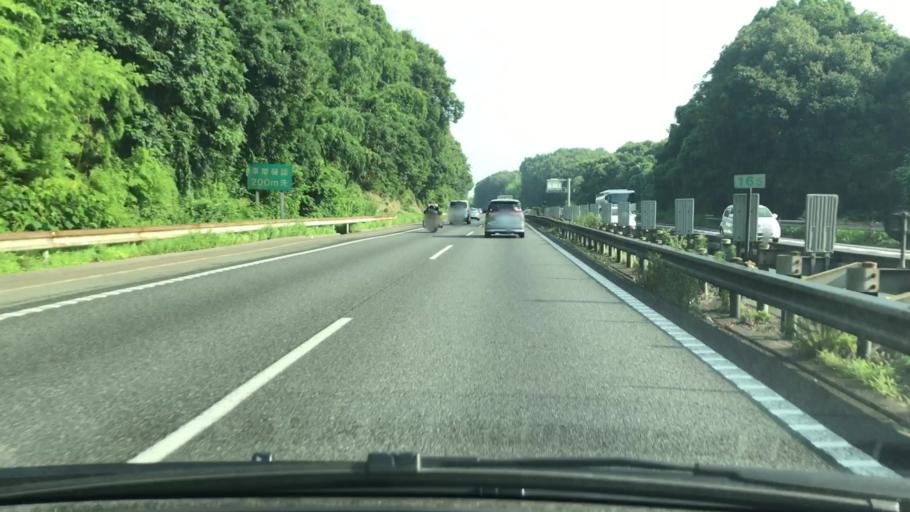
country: JP
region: Hyogo
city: Akashi
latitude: 34.6928
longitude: 134.9694
